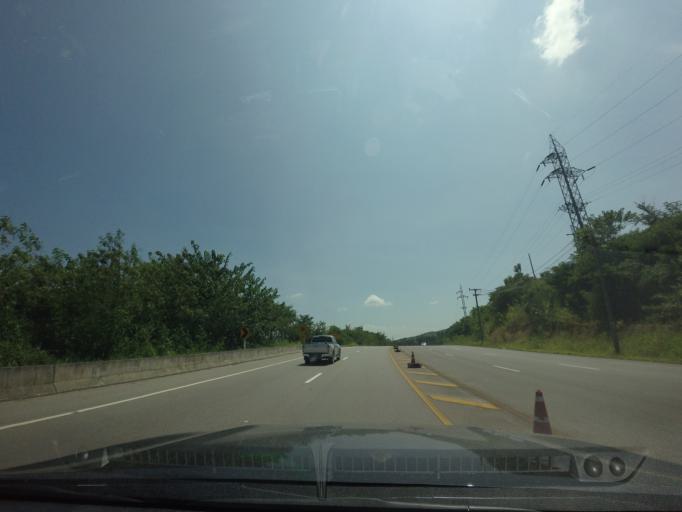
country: TH
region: Phetchabun
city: Lom Sak
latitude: 16.7702
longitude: 101.1361
